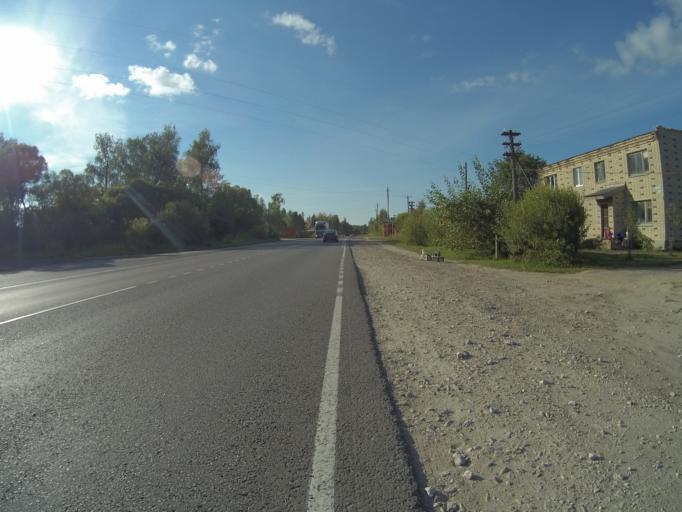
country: RU
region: Vladimir
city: Kommunar
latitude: 56.0450
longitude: 40.5400
